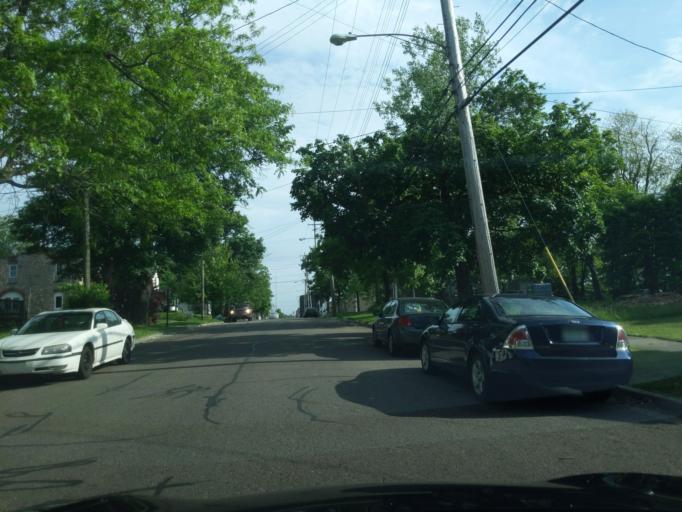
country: US
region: Michigan
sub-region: Ingham County
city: Lansing
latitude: 42.7320
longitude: -84.5412
